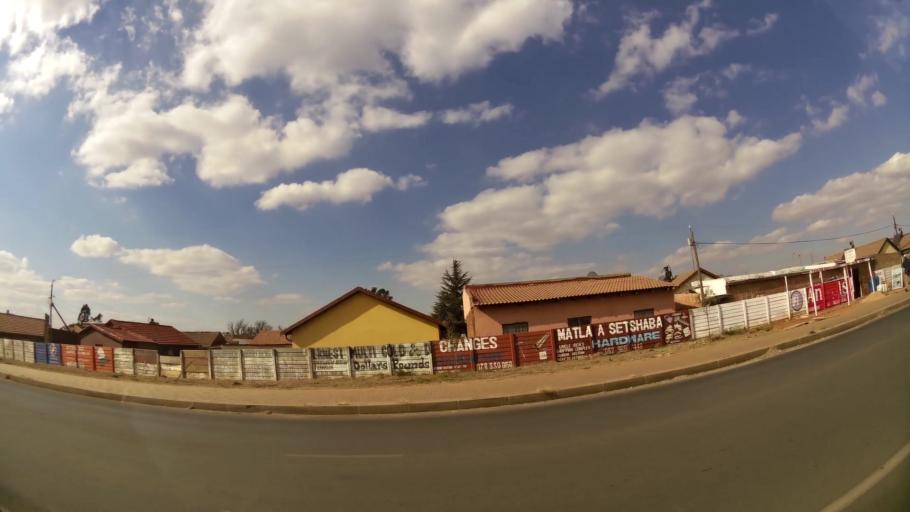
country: ZA
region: Gauteng
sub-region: Ekurhuleni Metropolitan Municipality
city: Tembisa
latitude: -25.9890
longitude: 28.2443
